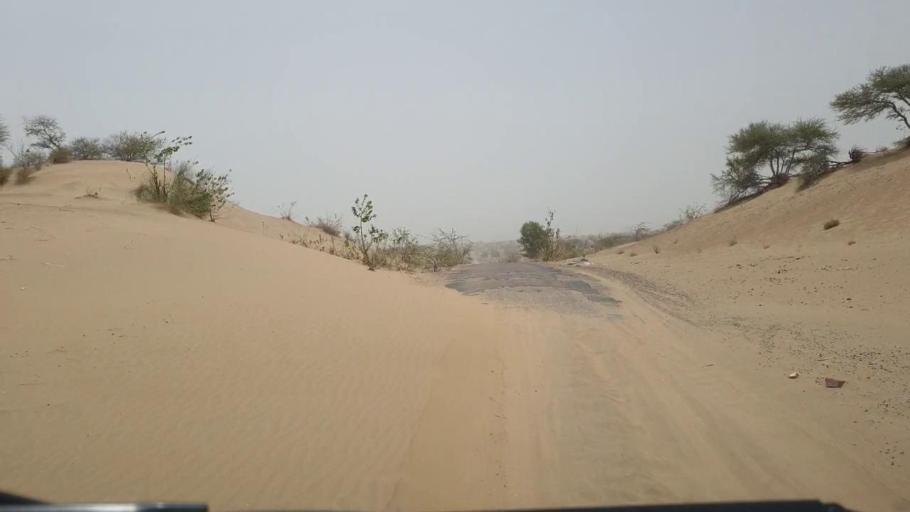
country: PK
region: Sindh
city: Naukot
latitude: 24.7608
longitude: 69.5482
